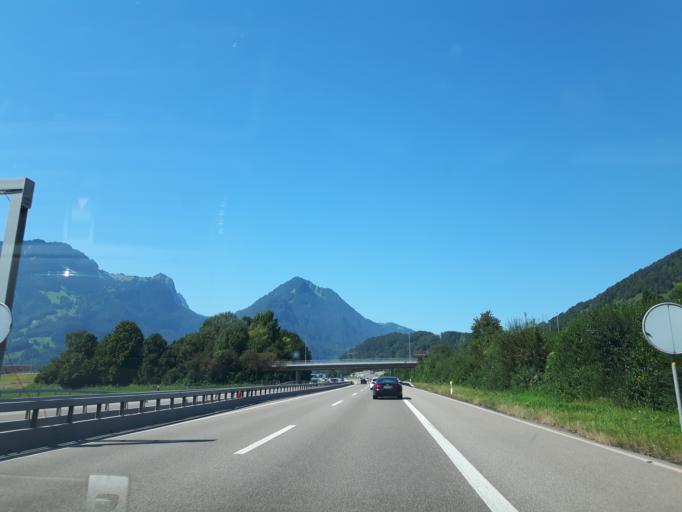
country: CH
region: Saint Gallen
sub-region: Wahlkreis See-Gaster
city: Weesen
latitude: 47.1277
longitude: 9.0953
